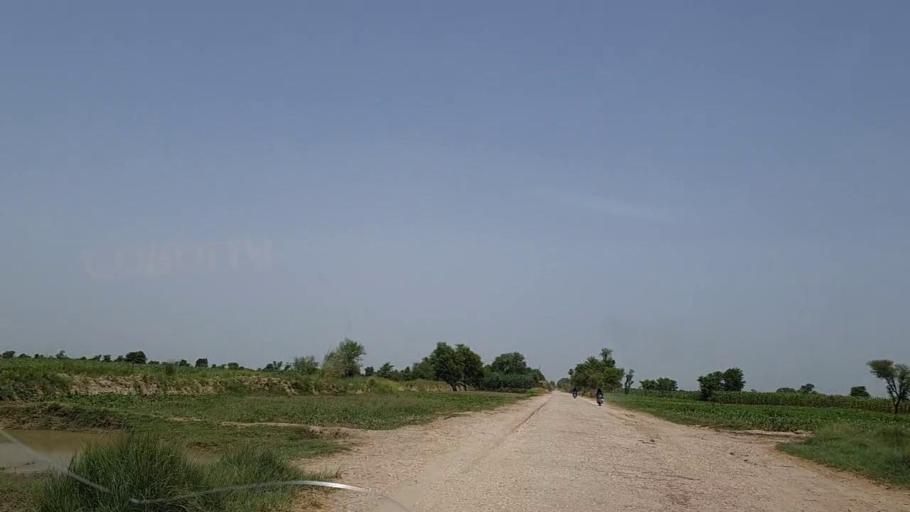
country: PK
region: Sindh
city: Tharu Shah
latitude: 26.9096
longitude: 68.0041
